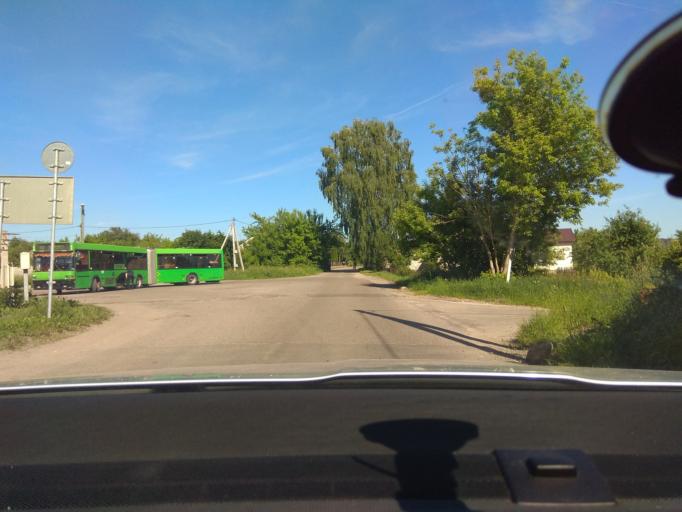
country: BY
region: Grodnenskaya
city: Hrodna
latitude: 53.6436
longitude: 23.7829
